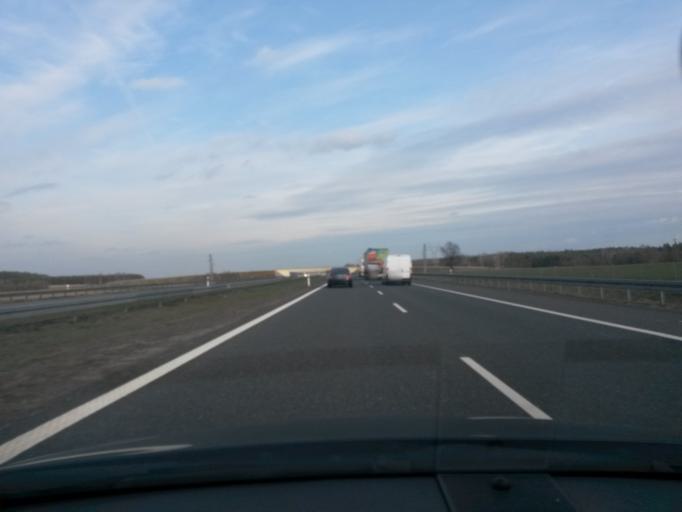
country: PL
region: Lodz Voivodeship
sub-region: Powiat zgierski
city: Ozorkow
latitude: 51.9293
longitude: 19.2949
